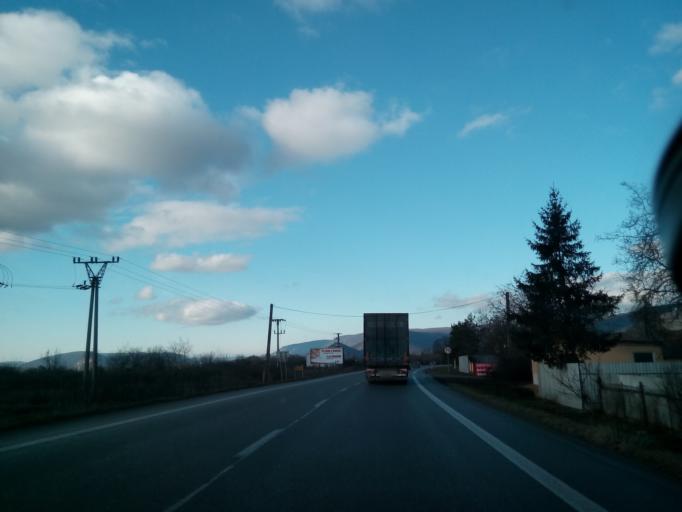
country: SK
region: Kosicky
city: Moldava nad Bodvou
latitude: 48.6059
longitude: 20.9560
